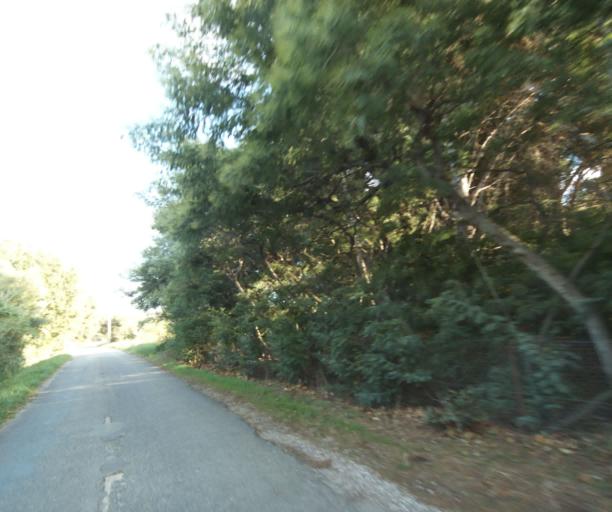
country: FR
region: Languedoc-Roussillon
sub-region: Departement des Pyrenees-Orientales
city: Argelers
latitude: 42.5646
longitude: 3.0126
